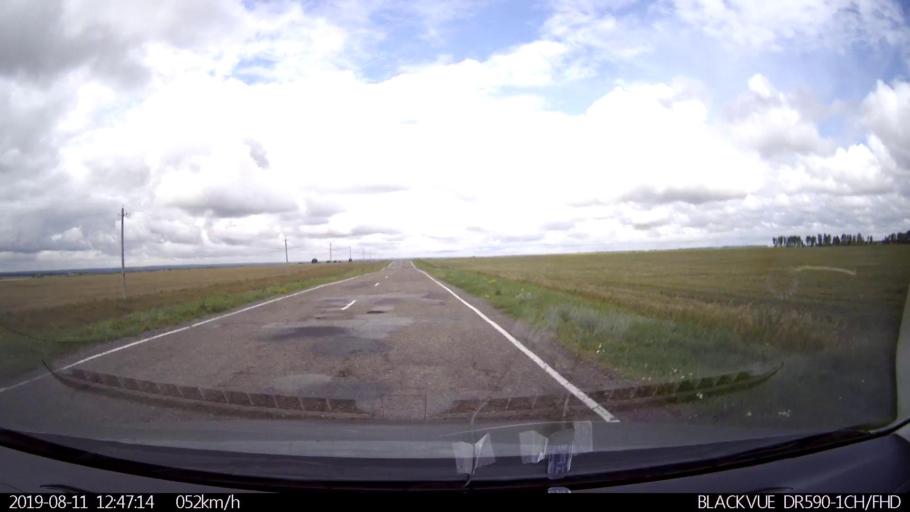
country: RU
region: Ulyanovsk
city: Ignatovka
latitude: 53.8686
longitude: 47.7105
